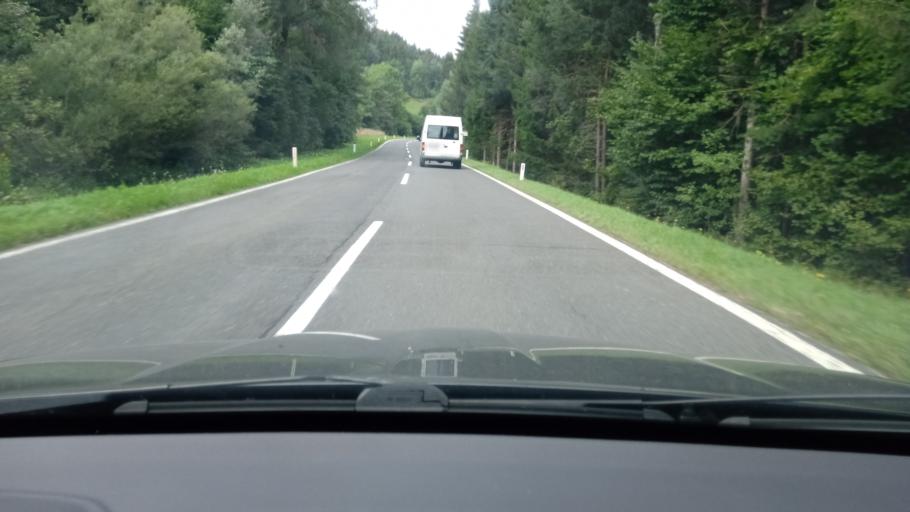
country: AT
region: Carinthia
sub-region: Politischer Bezirk Hermagor
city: Hermagor
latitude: 46.6484
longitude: 13.3319
